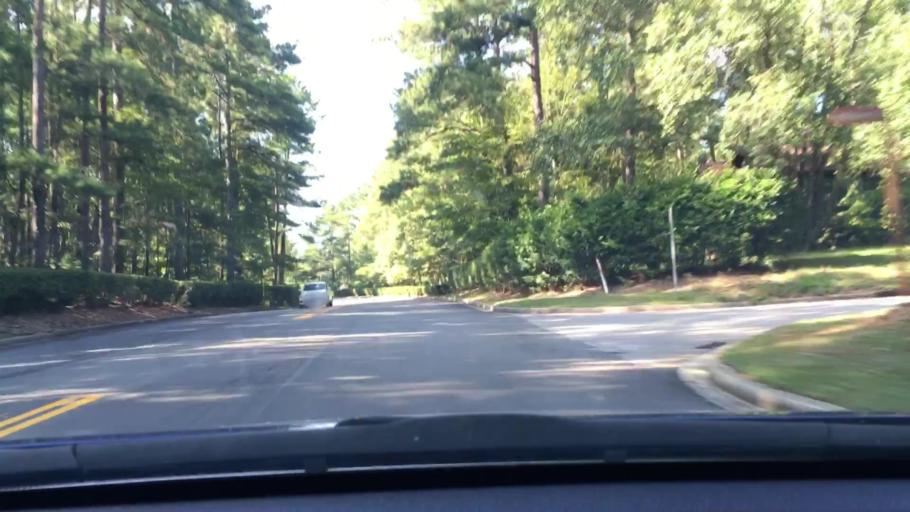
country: US
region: South Carolina
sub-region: Lexington County
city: Seven Oaks
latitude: 34.0800
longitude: -81.1398
